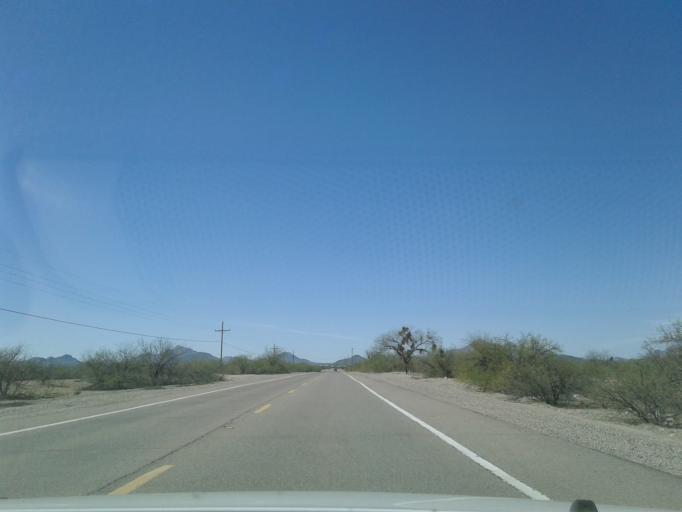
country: US
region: Arizona
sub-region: Pima County
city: Avra Valley
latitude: 32.3787
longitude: -111.3336
